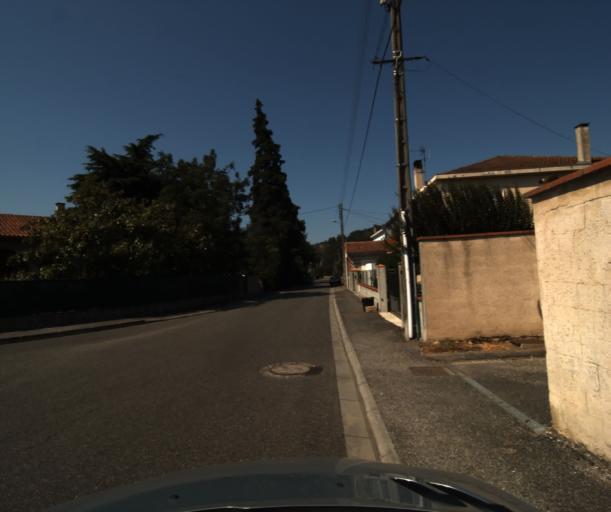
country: FR
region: Midi-Pyrenees
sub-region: Departement de la Haute-Garonne
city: Lacroix-Falgarde
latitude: 43.4905
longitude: 1.4078
